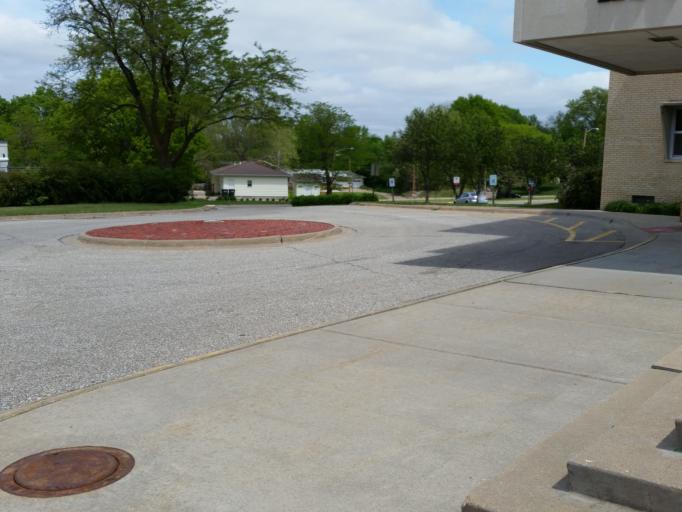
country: US
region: Kansas
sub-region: Riley County
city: Manhattan
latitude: 39.1886
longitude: -96.6004
